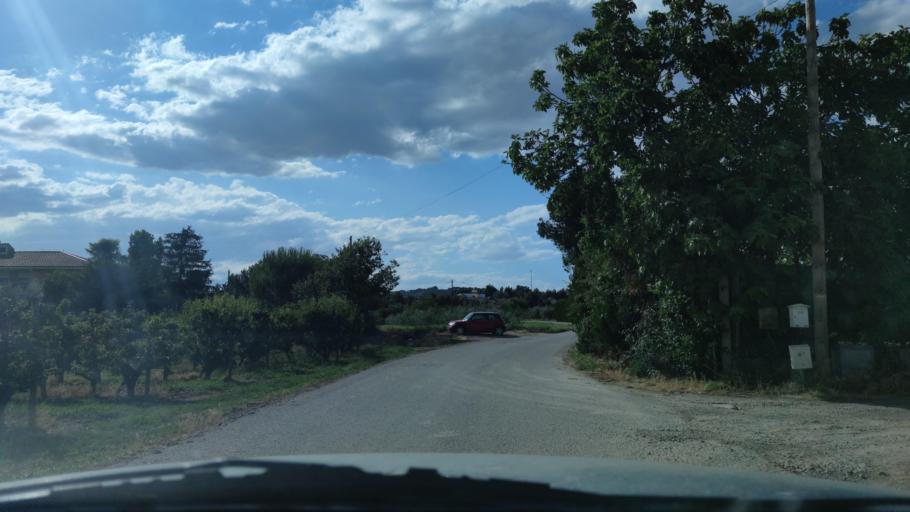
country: ES
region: Catalonia
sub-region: Provincia de Lleida
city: Alpicat
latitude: 41.6274
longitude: 0.5548
